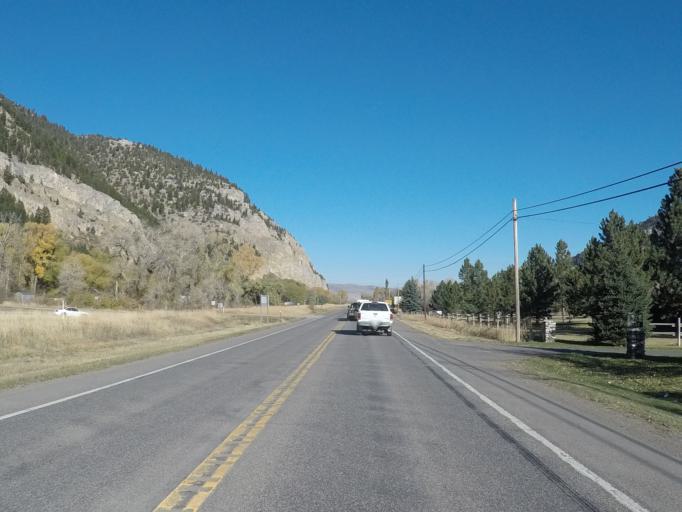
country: US
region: Montana
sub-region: Park County
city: Livingston
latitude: 45.6022
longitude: -110.5737
